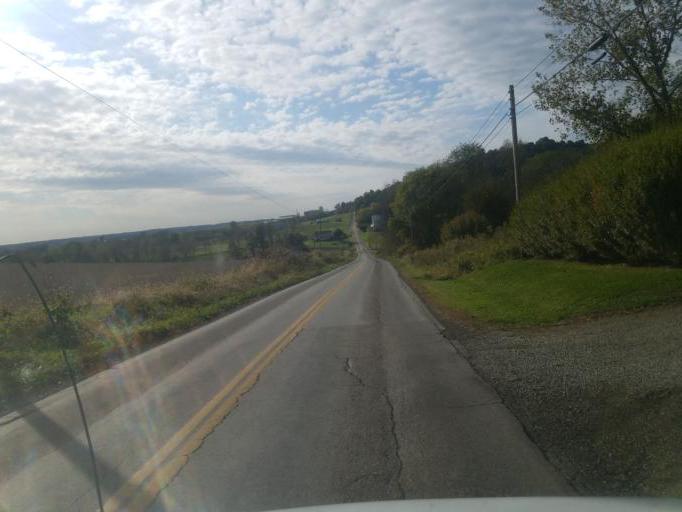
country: US
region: Ohio
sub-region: Wayne County
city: Shreve
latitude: 40.6713
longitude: -81.9204
